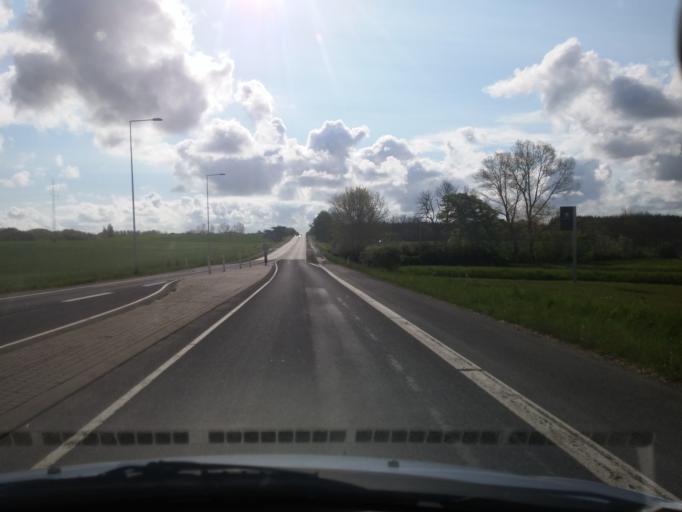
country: DK
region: South Denmark
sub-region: Nyborg Kommune
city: Ullerslev
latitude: 55.3616
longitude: 10.6795
